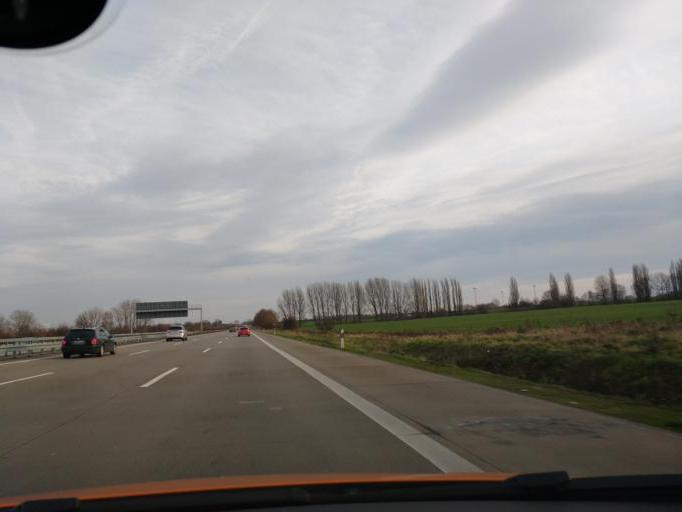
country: DE
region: Saxony-Anhalt
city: Erxleben
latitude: 52.1942
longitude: 11.2826
